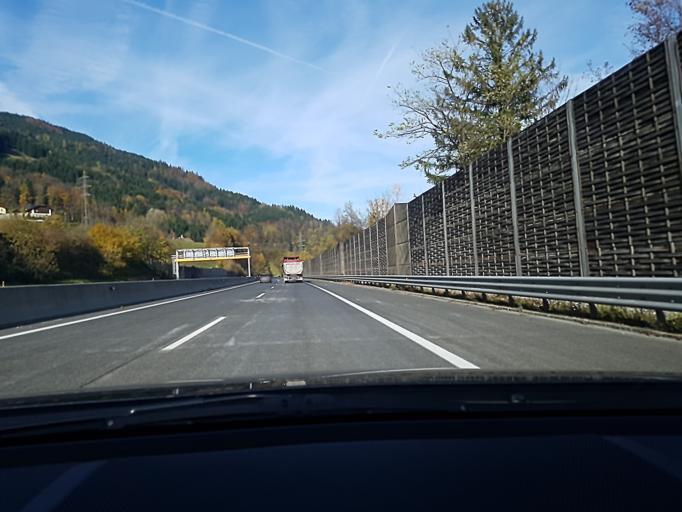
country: AT
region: Salzburg
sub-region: Politischer Bezirk Hallein
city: Kuchl
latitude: 47.6106
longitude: 13.1436
